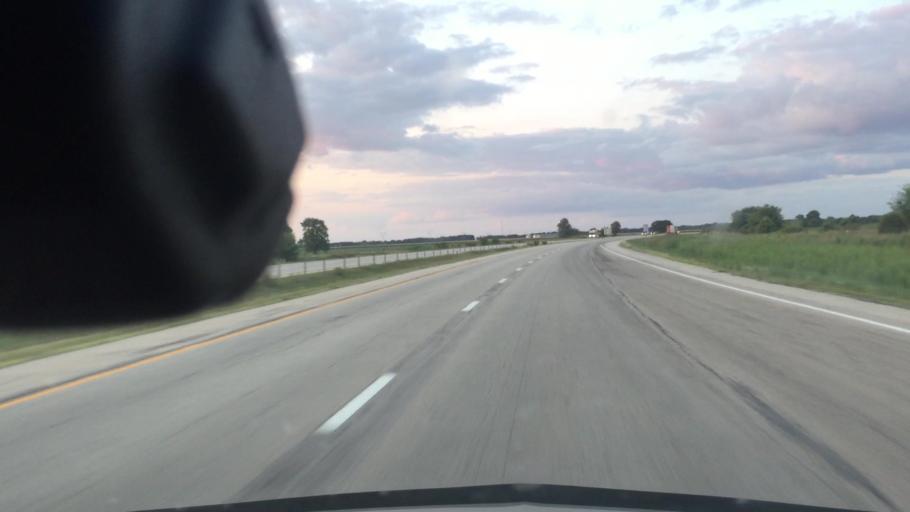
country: US
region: Illinois
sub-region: Grundy County
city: Gardner
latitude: 41.1908
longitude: -88.3198
